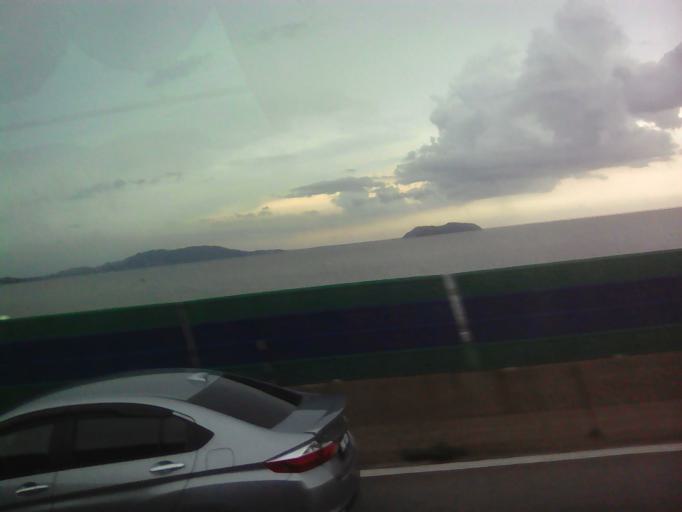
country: MY
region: Penang
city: Perai
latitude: 5.3523
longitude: 100.3789
